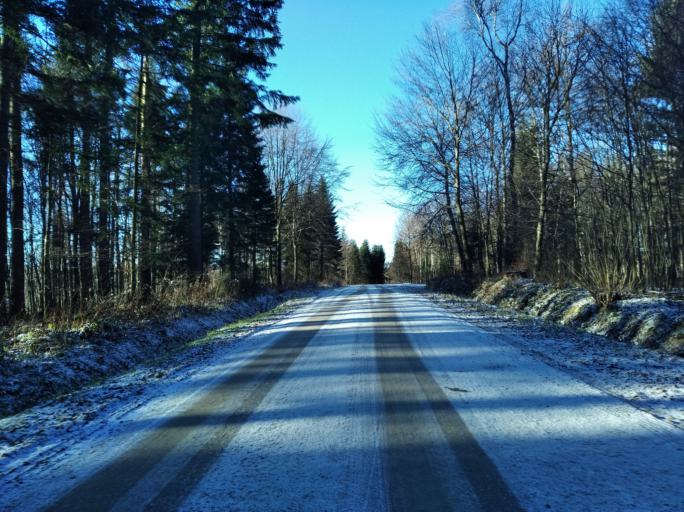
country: PL
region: Subcarpathian Voivodeship
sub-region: Powiat strzyzowski
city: Czudec
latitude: 49.9725
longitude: 21.7976
